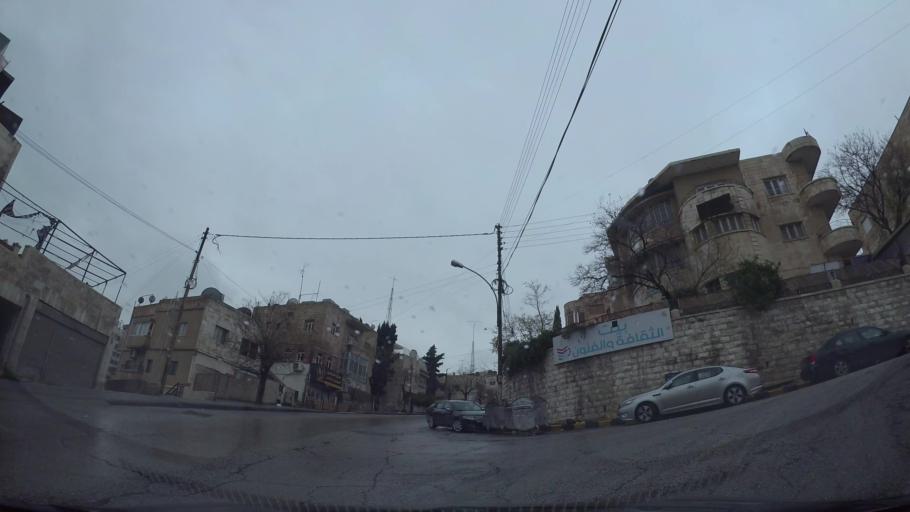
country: JO
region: Amman
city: Amman
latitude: 31.9601
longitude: 35.9198
